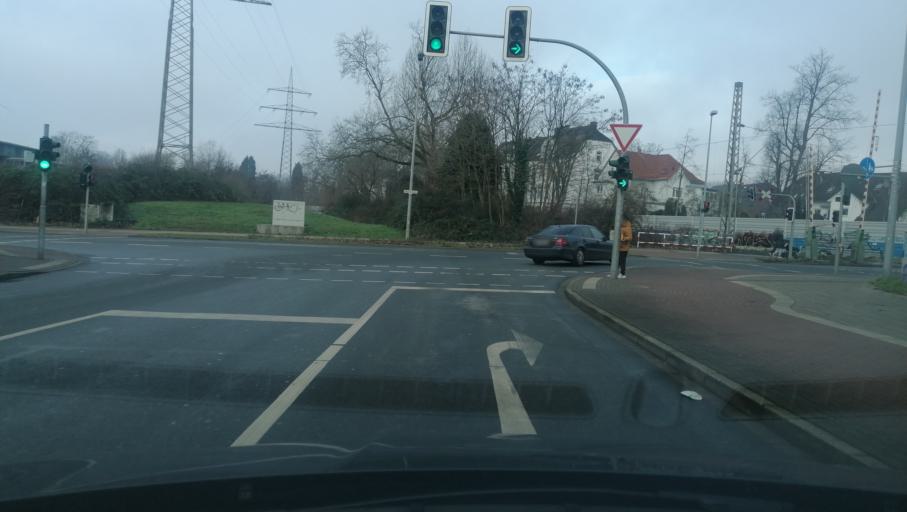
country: DE
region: North Rhine-Westphalia
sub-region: Regierungsbezirk Munster
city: Gelsenkirchen
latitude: 51.5243
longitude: 7.1050
